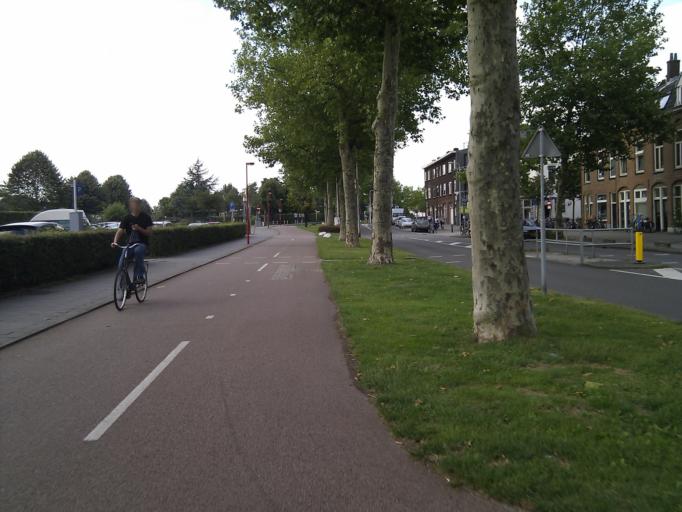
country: NL
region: Utrecht
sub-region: Gemeente Utrecht
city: Utrecht
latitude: 52.0989
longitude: 5.1290
